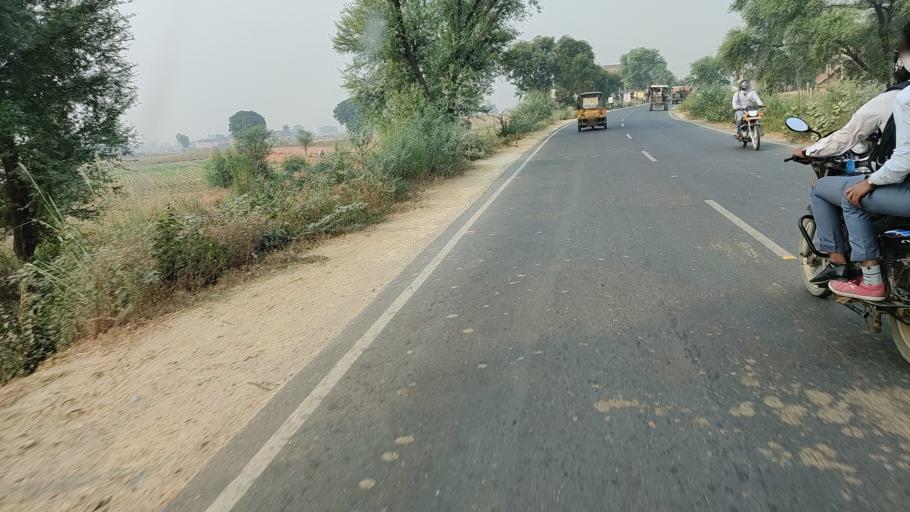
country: IN
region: Uttar Pradesh
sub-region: Mathura
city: Vrindavan
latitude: 27.5580
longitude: 77.7197
